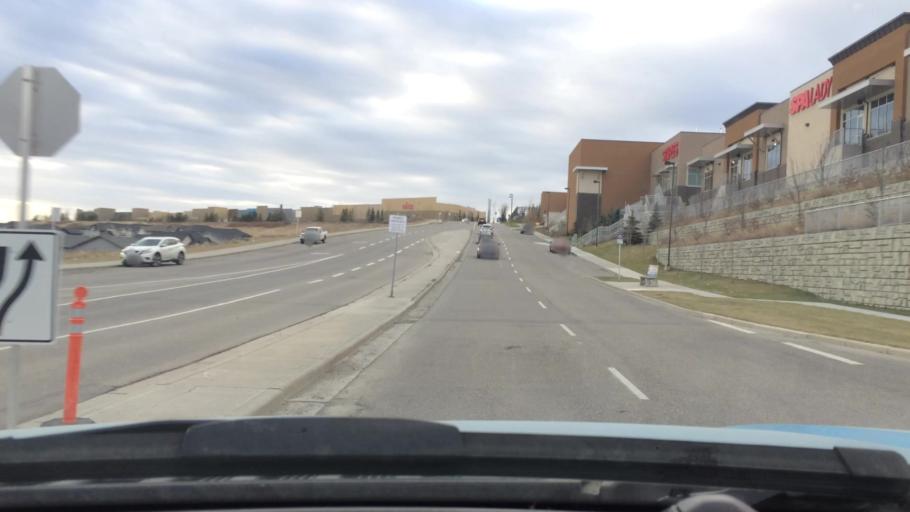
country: CA
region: Alberta
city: Calgary
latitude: 51.1625
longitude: -114.1597
